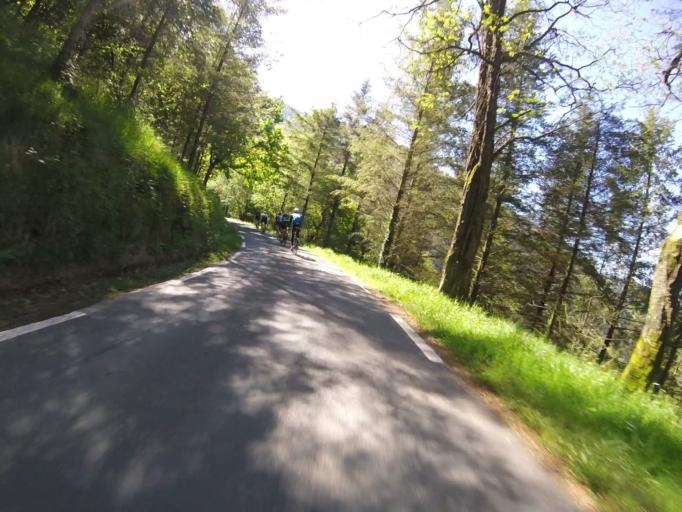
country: ES
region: Basque Country
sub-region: Provincia de Guipuzcoa
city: Errezil
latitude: 43.1905
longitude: -2.1939
